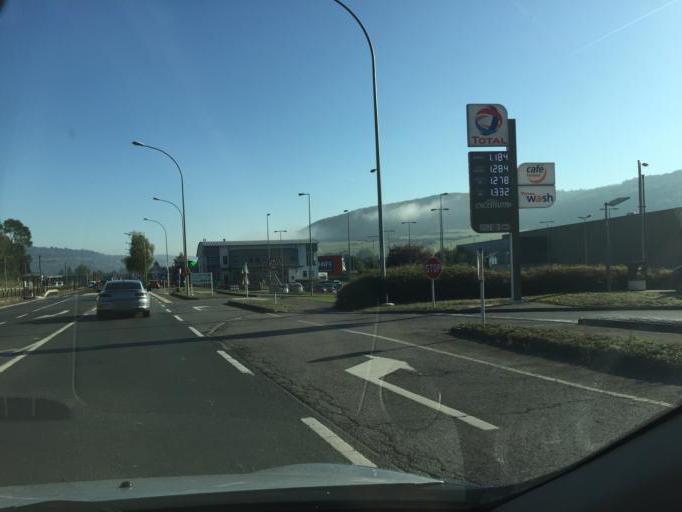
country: LU
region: Diekirch
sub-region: Canton de Diekirch
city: Erpeldange
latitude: 49.8507
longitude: 6.1255
